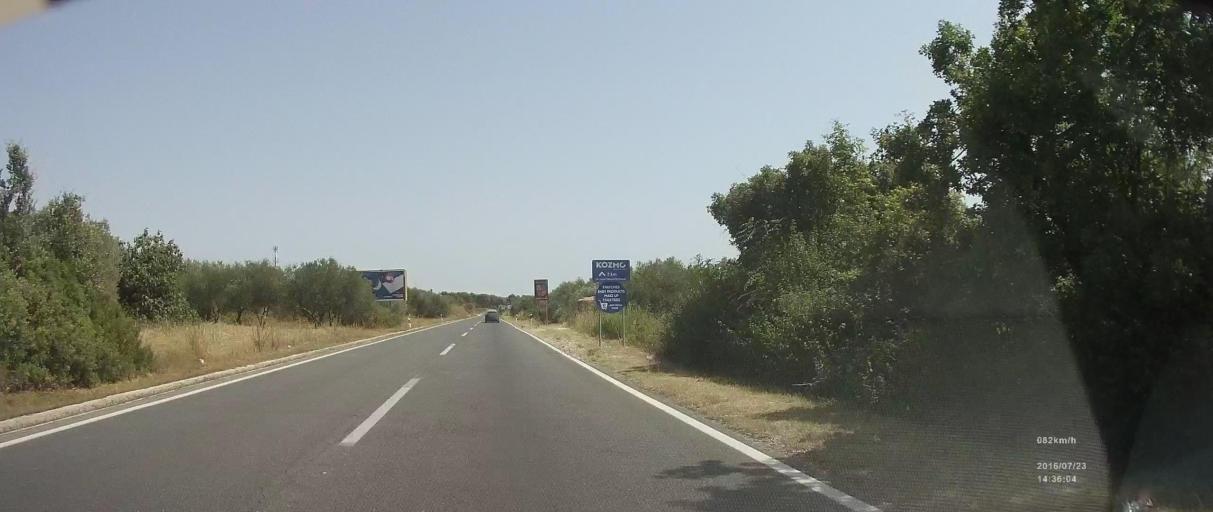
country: HR
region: Zadarska
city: Sveti Filip i Jakov
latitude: 43.9547
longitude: 15.4412
